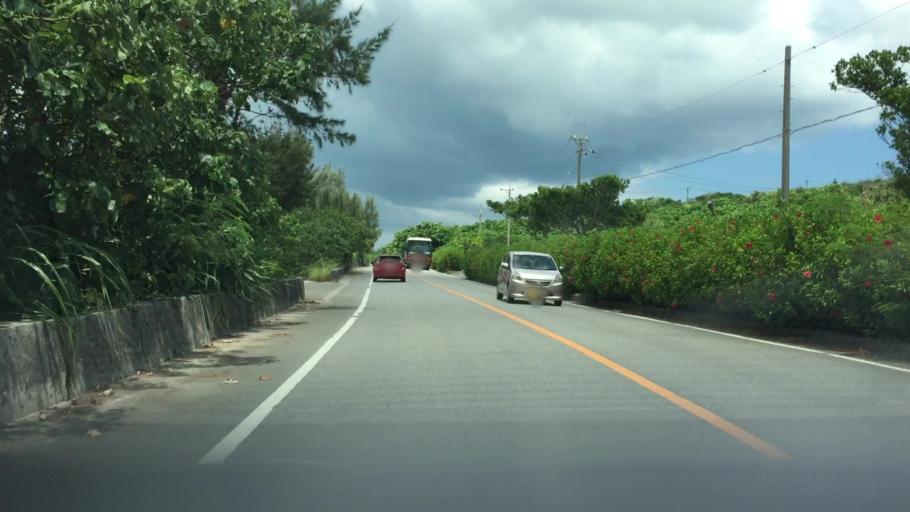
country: JP
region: Okinawa
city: Ishigaki
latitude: 24.4253
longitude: 124.1286
